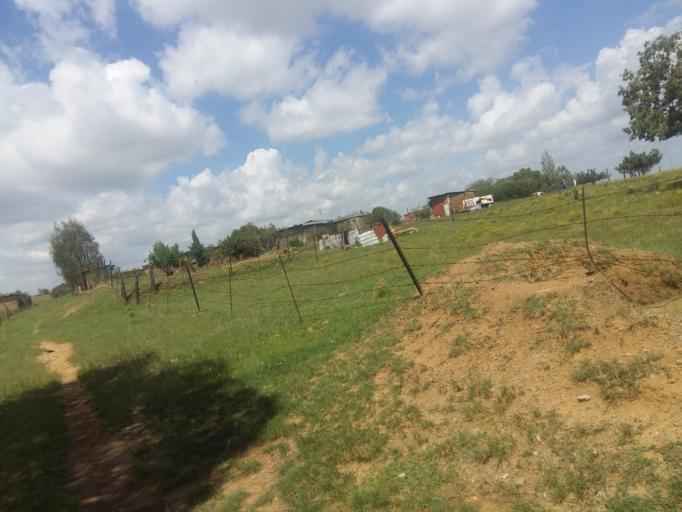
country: LS
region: Mafeteng
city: Mafeteng
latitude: -29.7479
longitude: 27.1142
